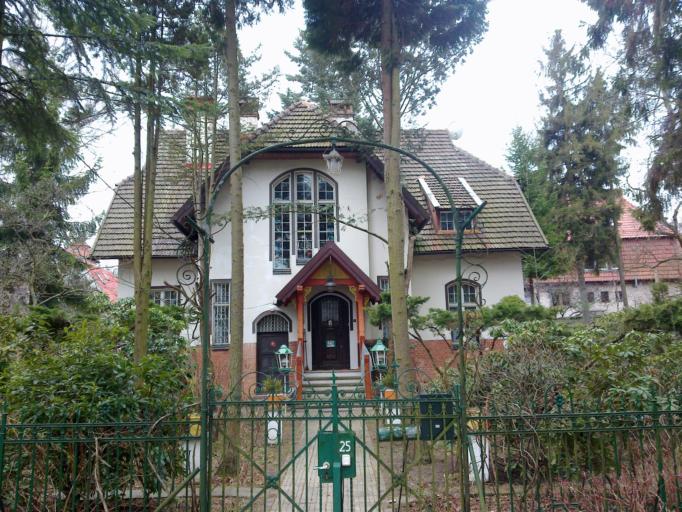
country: PL
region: Pomeranian Voivodeship
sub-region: Sopot
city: Sopot
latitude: 54.4405
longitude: 18.5539
